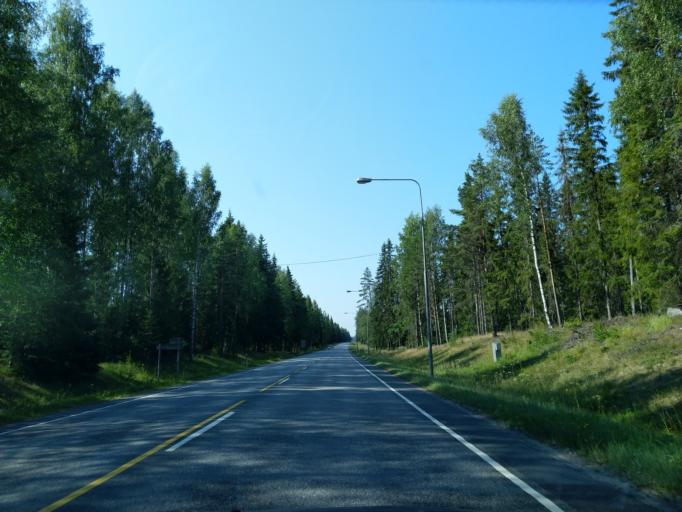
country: FI
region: Satakunta
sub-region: Pori
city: Pomarkku
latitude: 61.6589
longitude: 21.9673
